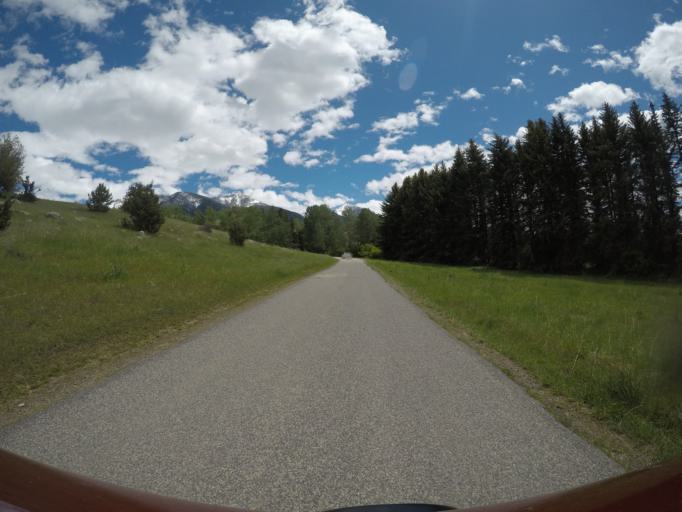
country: US
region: Montana
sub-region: Park County
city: Livingston
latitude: 45.4967
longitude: -110.5682
